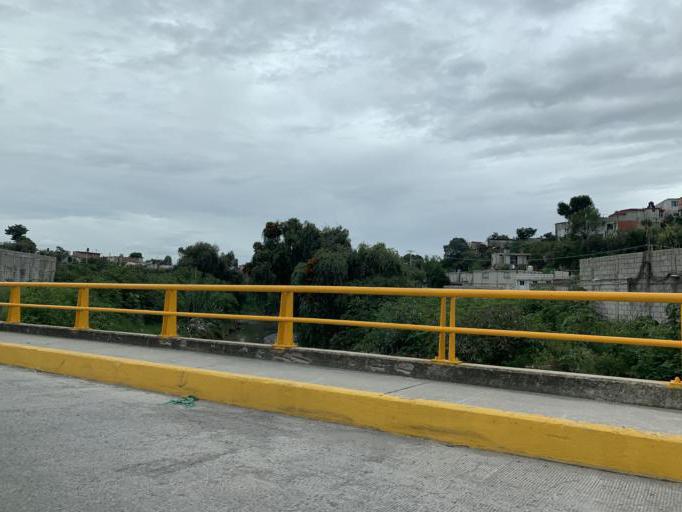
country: MX
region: Puebla
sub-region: Puebla
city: Galaxia la Calera
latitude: 18.9954
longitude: -98.1870
